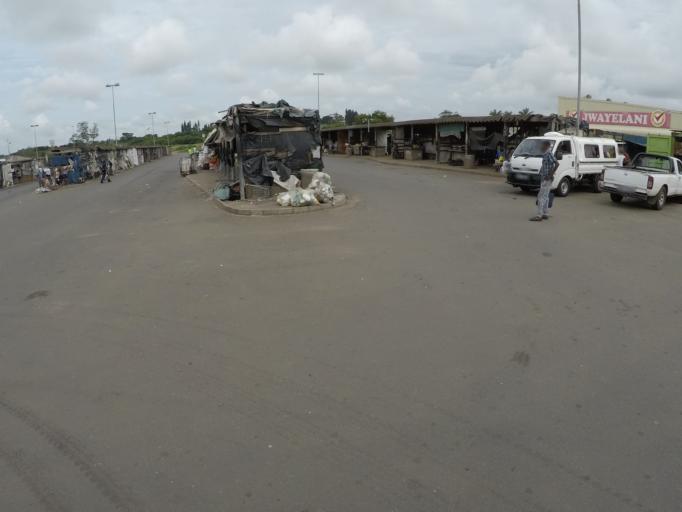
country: ZA
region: KwaZulu-Natal
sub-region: uThungulu District Municipality
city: Empangeni
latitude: -28.7743
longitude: 31.9031
